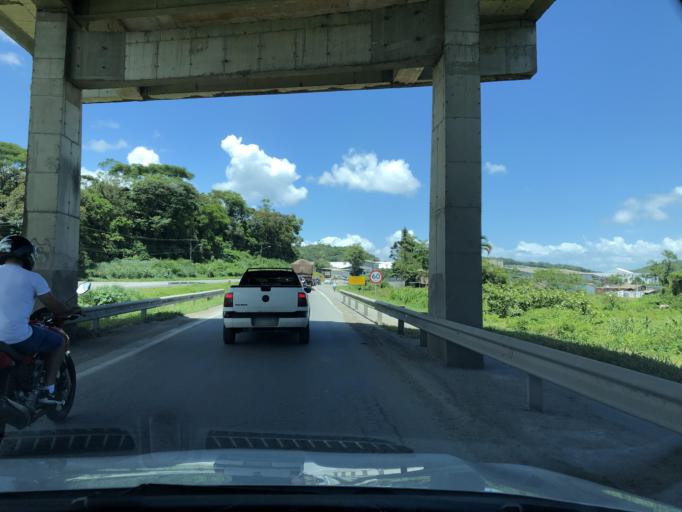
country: BR
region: Santa Catarina
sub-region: Sao Francisco Do Sul
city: Sao Francisco do Sul
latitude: -26.2524
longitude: -48.6119
